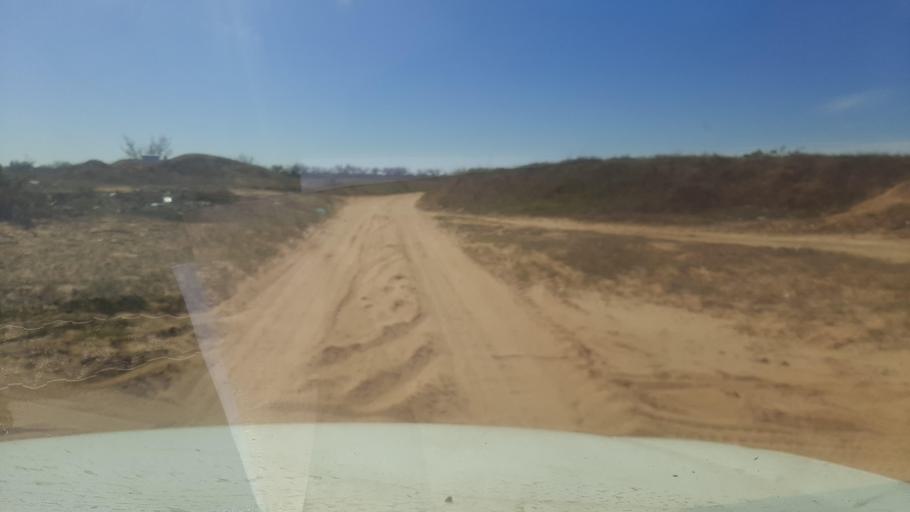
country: TN
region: Safaqis
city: Sfax
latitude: 34.8288
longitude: 10.5556
